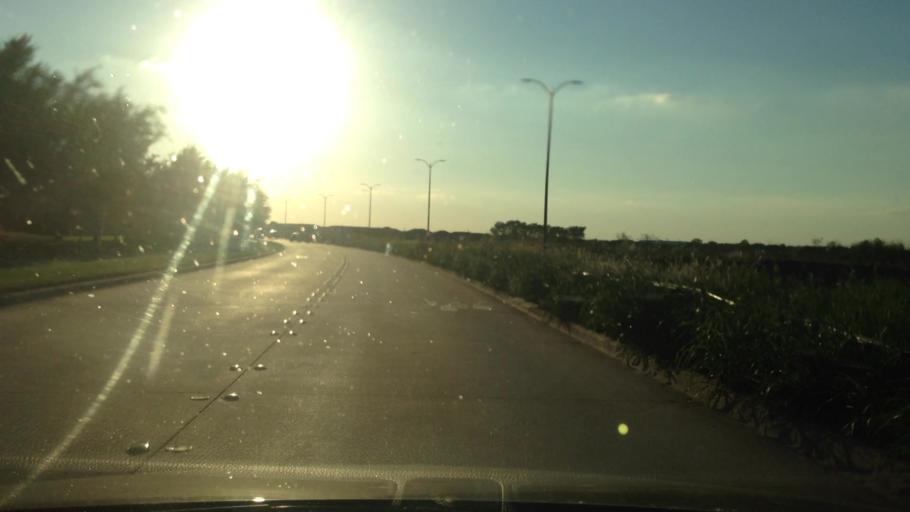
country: US
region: Texas
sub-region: Denton County
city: Little Elm
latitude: 33.1461
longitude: -96.9011
